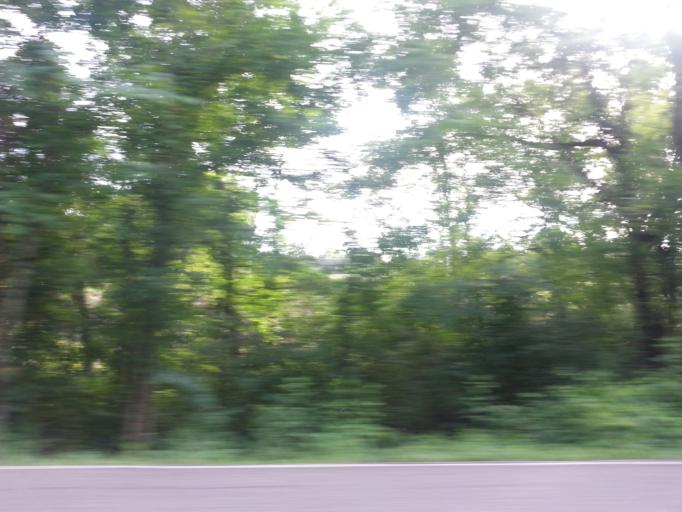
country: US
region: Tennessee
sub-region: Knox County
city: Farragut
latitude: 35.9106
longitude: -84.0777
